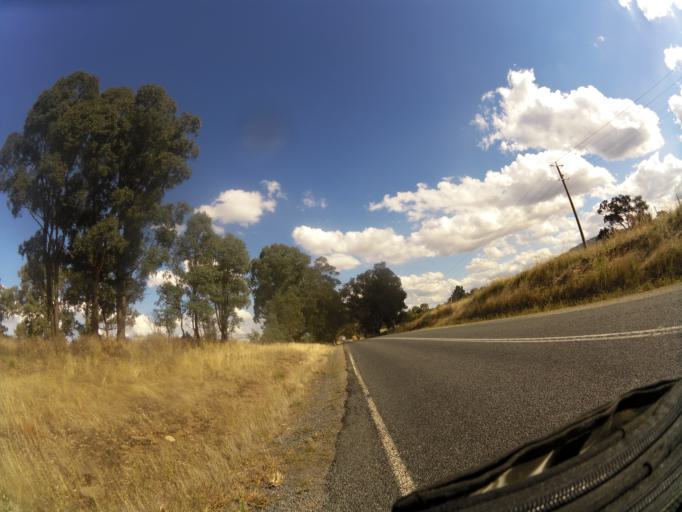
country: AU
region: Victoria
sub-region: Mansfield
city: Mansfield
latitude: -36.9295
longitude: 146.0009
